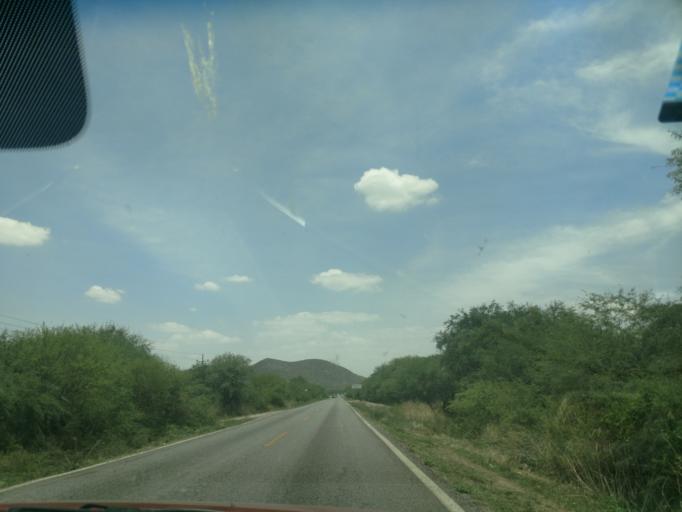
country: MX
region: San Luis Potosi
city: Ciudad Fernandez
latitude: 22.0085
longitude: -100.1529
